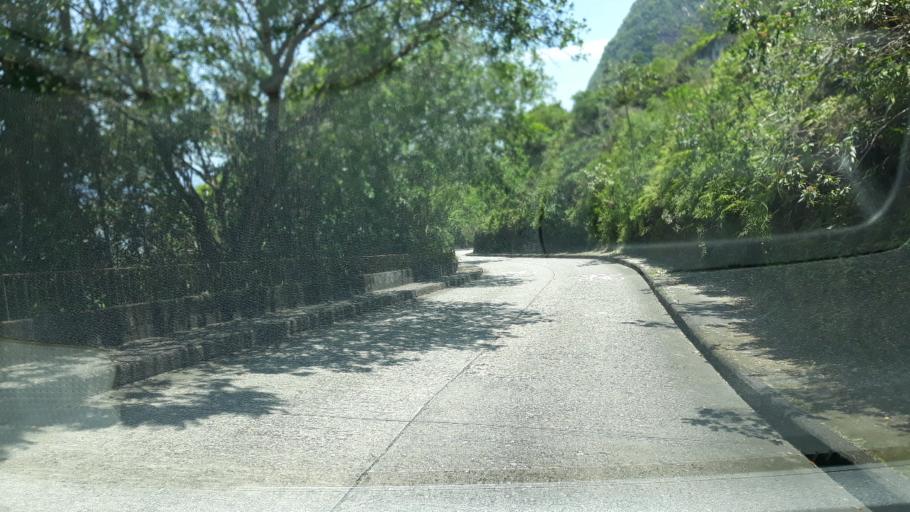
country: BR
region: Rio de Janeiro
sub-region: Rio De Janeiro
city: Rio de Janeiro
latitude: -22.9464
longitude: -43.1975
